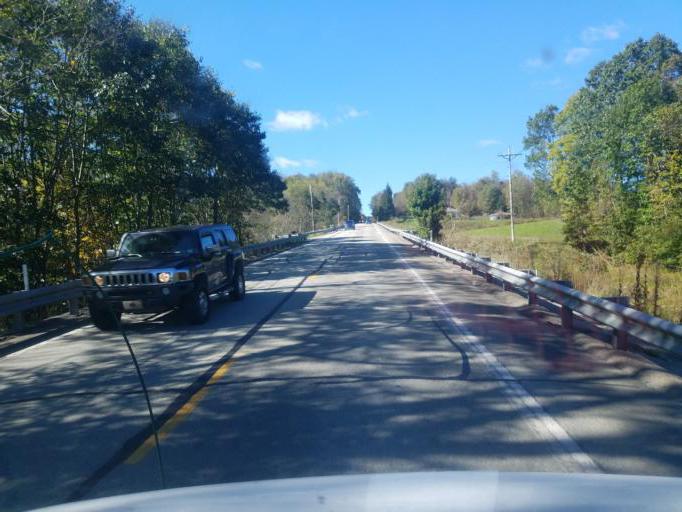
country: US
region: Pennsylvania
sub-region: Somerset County
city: Boswell
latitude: 40.1672
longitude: -79.0958
